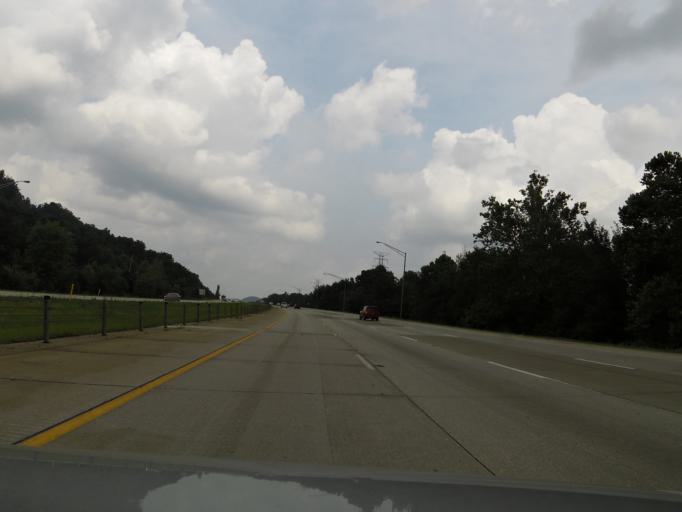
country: US
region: Kentucky
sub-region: Bullitt County
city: Lebanon Junction
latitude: 37.8322
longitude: -85.7179
